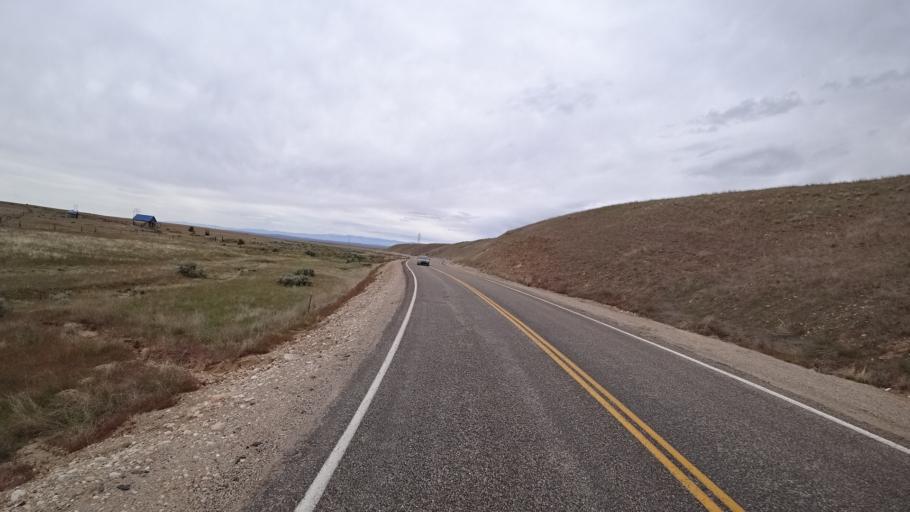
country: US
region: Idaho
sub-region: Ada County
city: Boise
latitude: 43.4755
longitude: -116.0550
